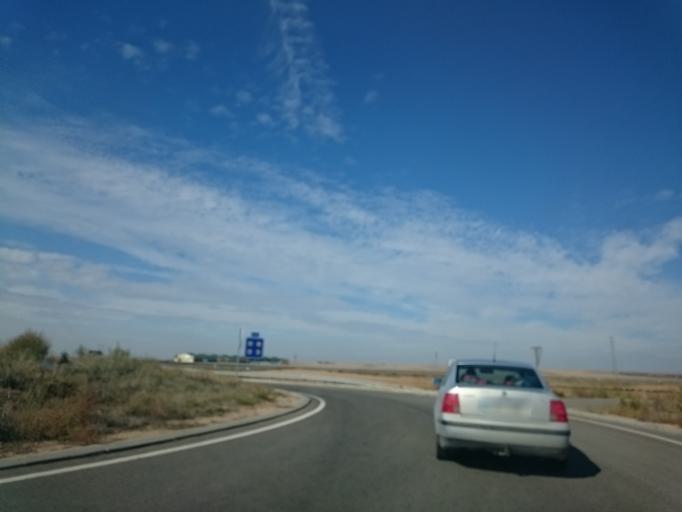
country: ES
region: Catalonia
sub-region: Provincia de Lleida
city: Alguaire
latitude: 41.7335
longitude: 0.5629
